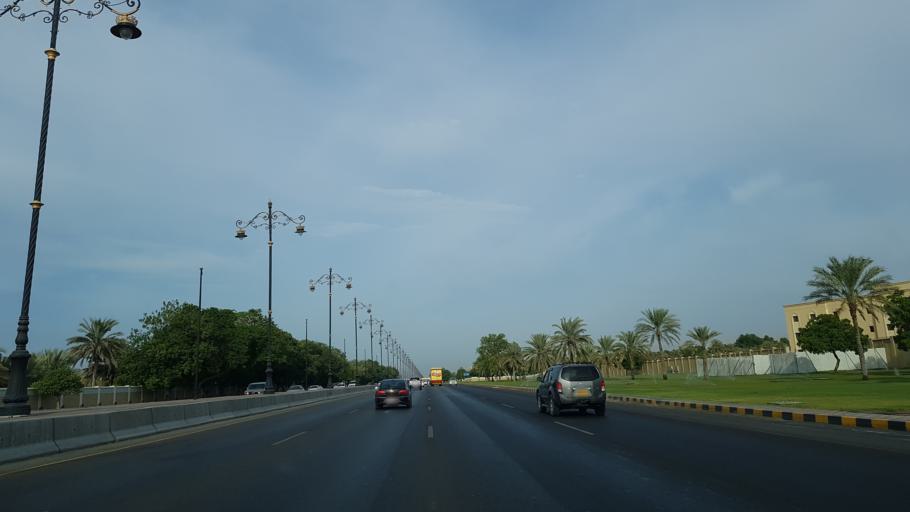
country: OM
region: Muhafazat Masqat
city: Bawshar
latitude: 23.5844
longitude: 58.2794
